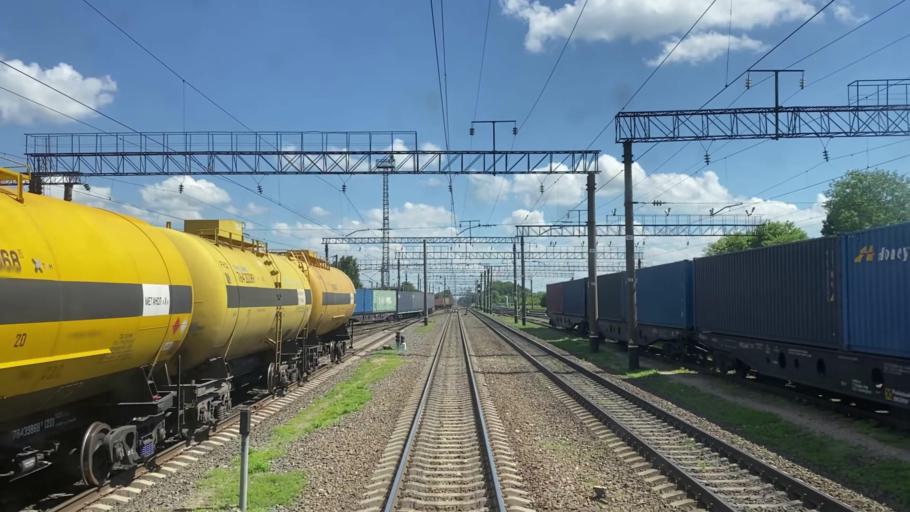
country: BY
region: Brest
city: Baranovichi
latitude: 53.1423
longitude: 26.0184
